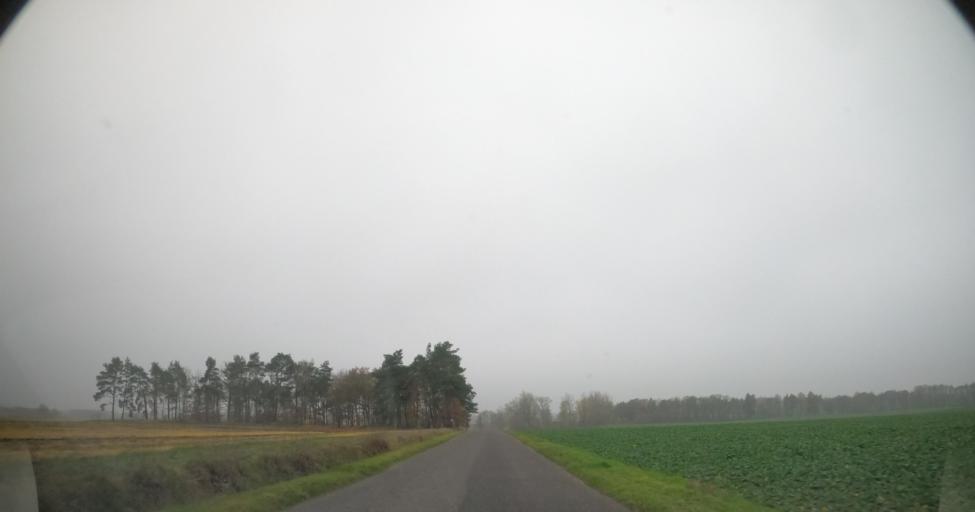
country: PL
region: West Pomeranian Voivodeship
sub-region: Powiat drawski
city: Drawsko Pomorskie
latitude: 53.6045
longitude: 15.7386
